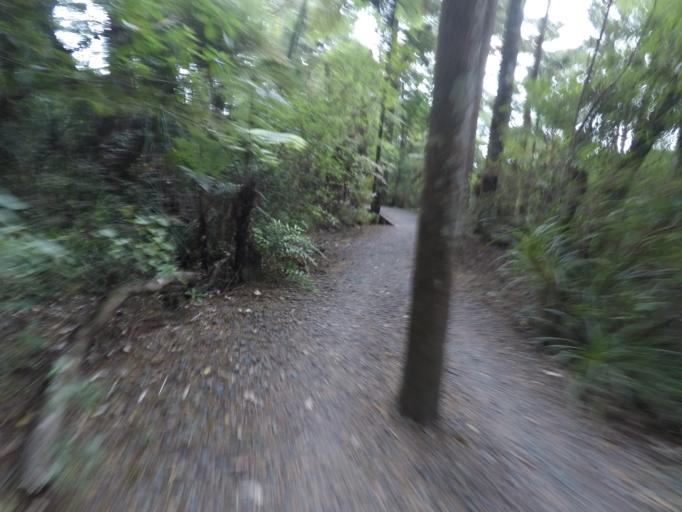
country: NZ
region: Northland
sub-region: Whangarei
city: Whangarei
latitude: -35.7139
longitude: 174.3306
